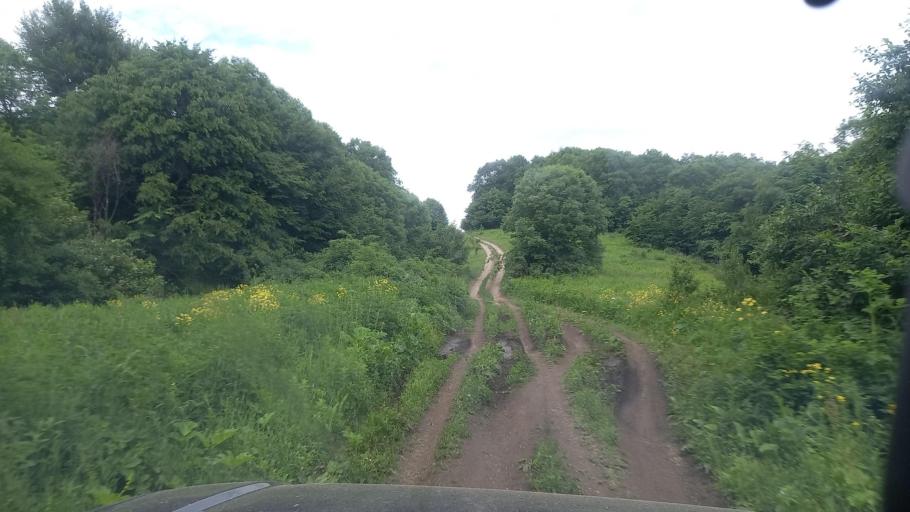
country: RU
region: Karachayevo-Cherkesiya
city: Pregradnaya
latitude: 44.0290
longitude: 41.3050
